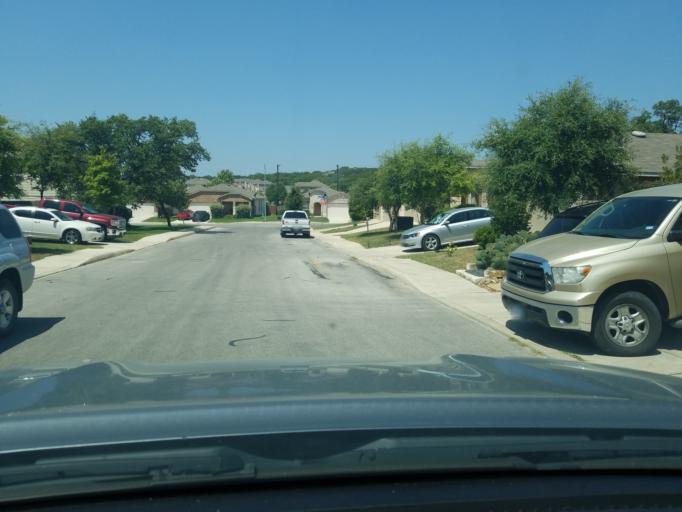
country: US
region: Texas
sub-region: Bexar County
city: Timberwood Park
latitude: 29.7045
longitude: -98.4808
